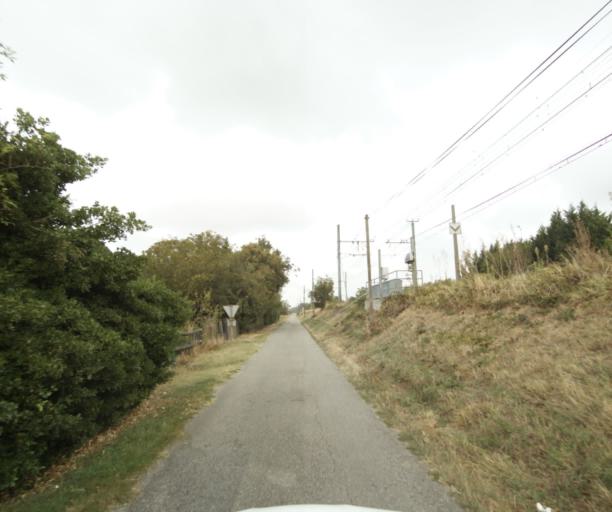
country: FR
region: Midi-Pyrenees
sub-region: Departement de la Haute-Garonne
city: Villefranche-de-Lauragais
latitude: 43.4007
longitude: 1.7123
